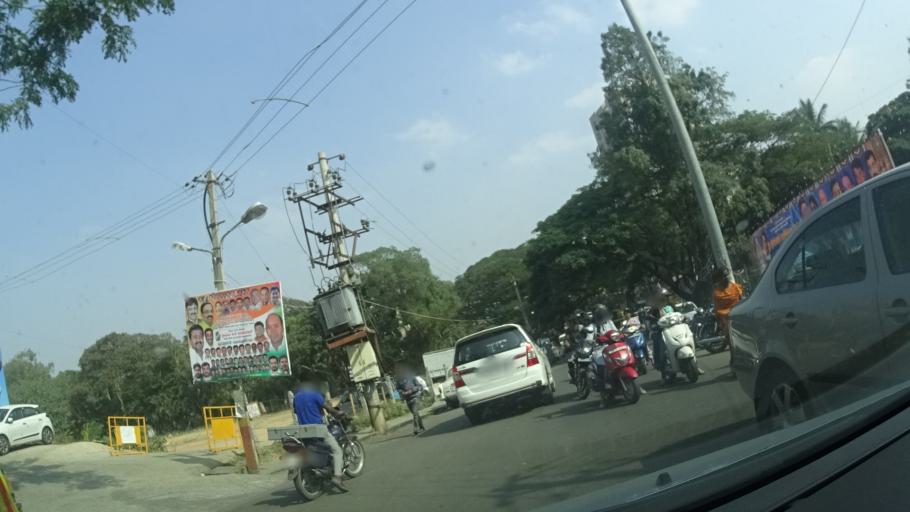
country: IN
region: Karnataka
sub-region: Bangalore Urban
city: Bangalore
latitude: 12.9485
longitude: 77.5582
